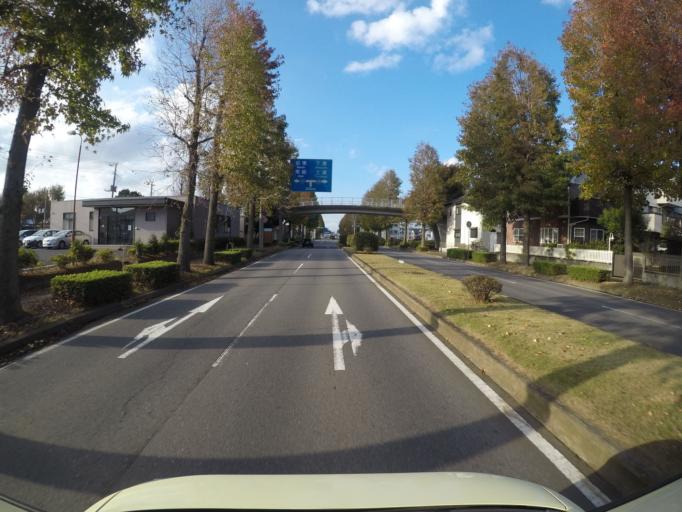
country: JP
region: Ibaraki
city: Naka
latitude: 36.0700
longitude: 140.0985
